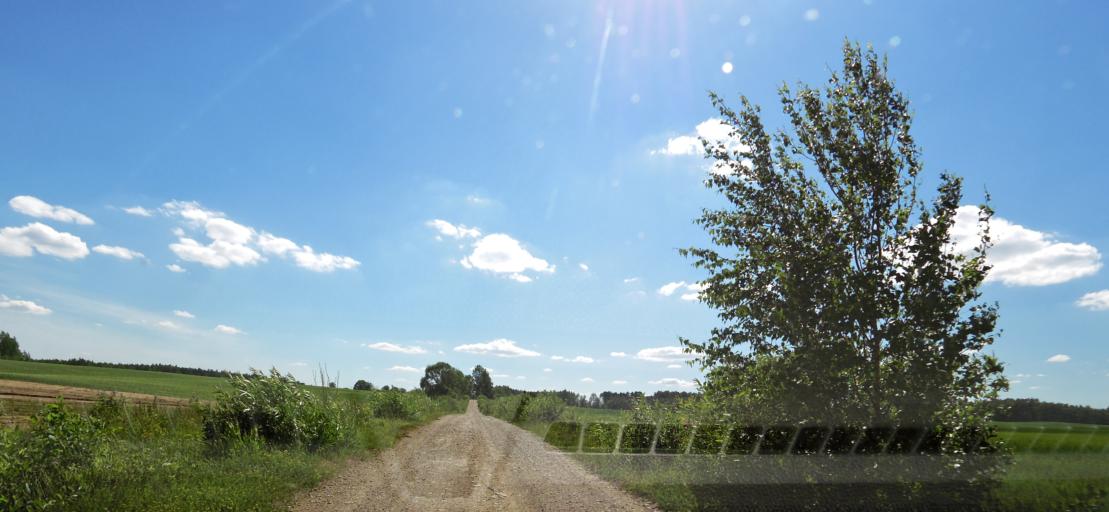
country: LT
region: Vilnius County
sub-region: Vilnius
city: Fabijoniskes
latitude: 54.8446
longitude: 25.3356
